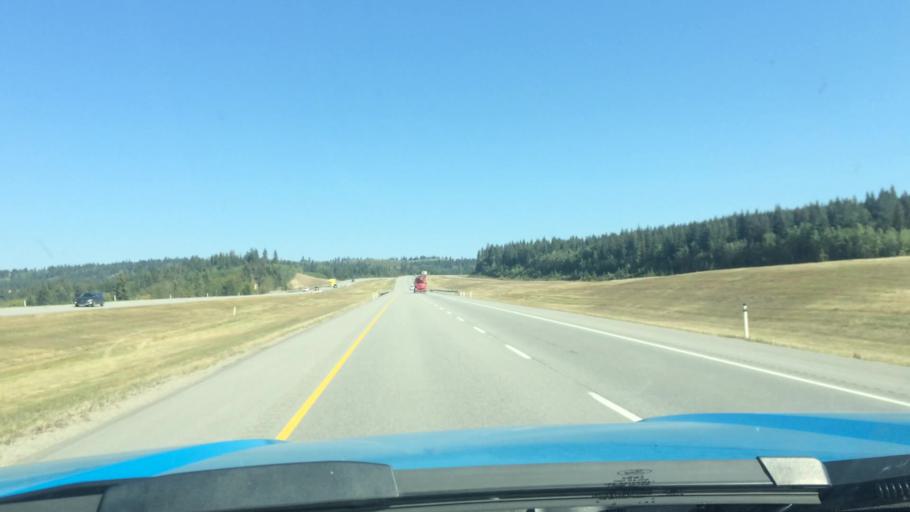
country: CA
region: Alberta
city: Cochrane
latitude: 51.1614
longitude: -114.7736
